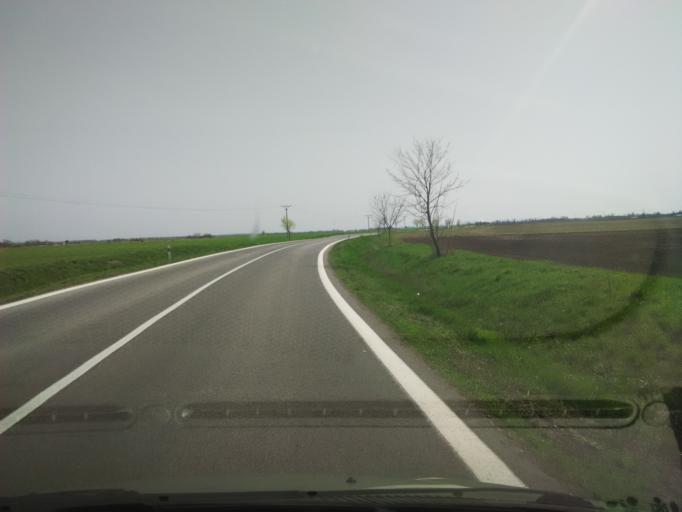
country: SK
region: Nitriansky
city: Surany
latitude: 48.0530
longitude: 18.1102
